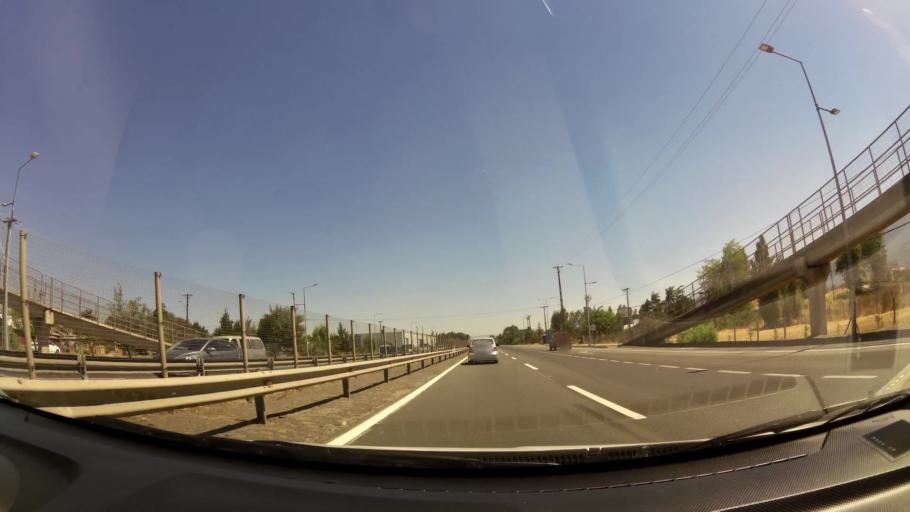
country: CL
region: O'Higgins
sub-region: Provincia de Cachapoal
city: Rengo
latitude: -34.5409
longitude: -70.9484
